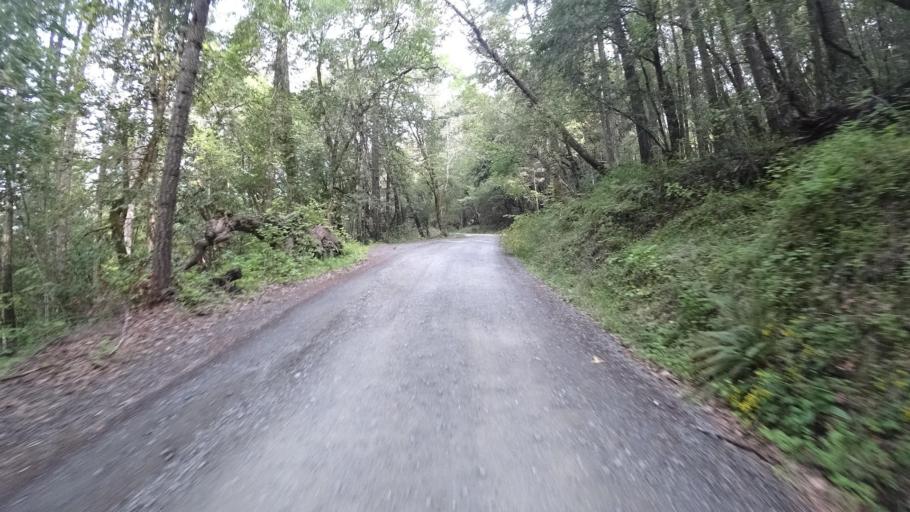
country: US
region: California
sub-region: Humboldt County
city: Redway
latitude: 40.2409
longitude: -123.8130
